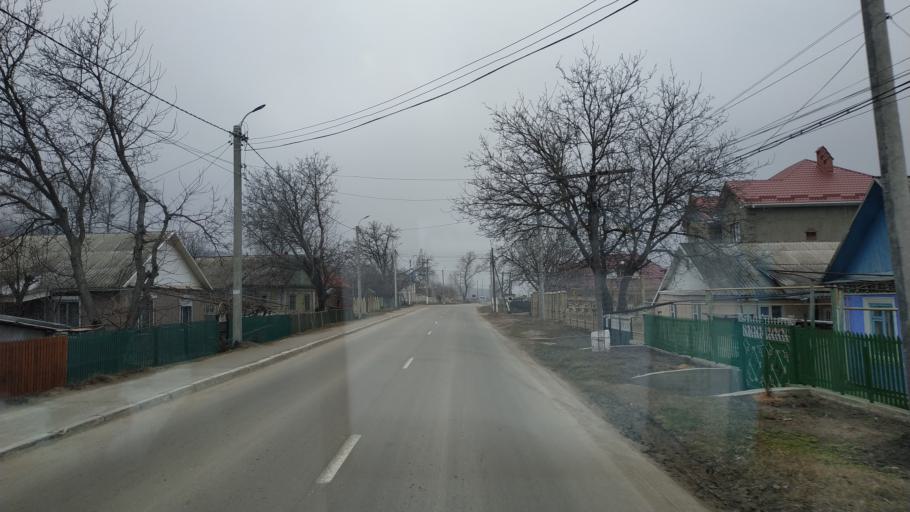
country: MD
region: Hincesti
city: Hincesti
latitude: 46.8418
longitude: 28.5807
